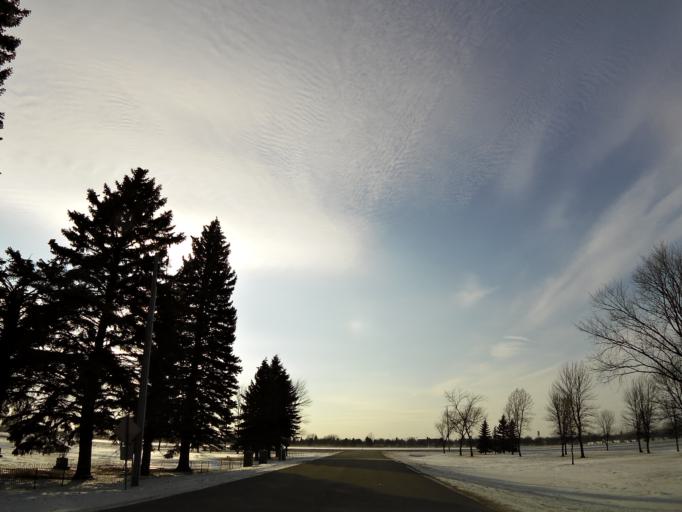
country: US
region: North Dakota
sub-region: Walsh County
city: Grafton
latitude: 48.4170
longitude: -97.3889
